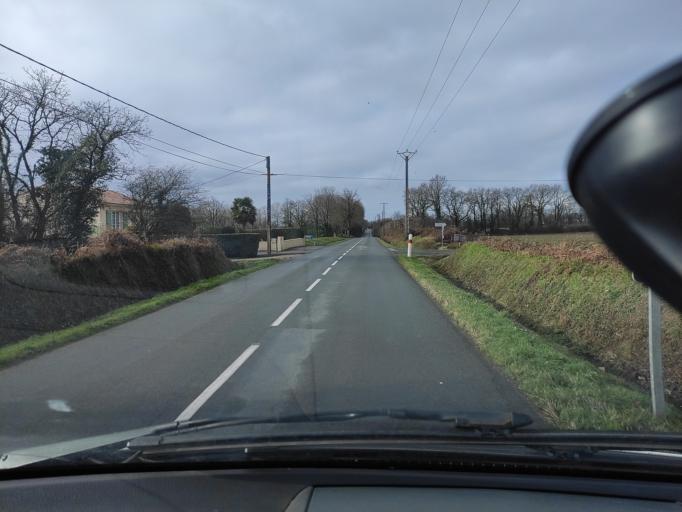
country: FR
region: Pays de la Loire
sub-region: Departement de la Vendee
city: La Boissiere-des-Landes
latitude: 46.5683
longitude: -1.4834
